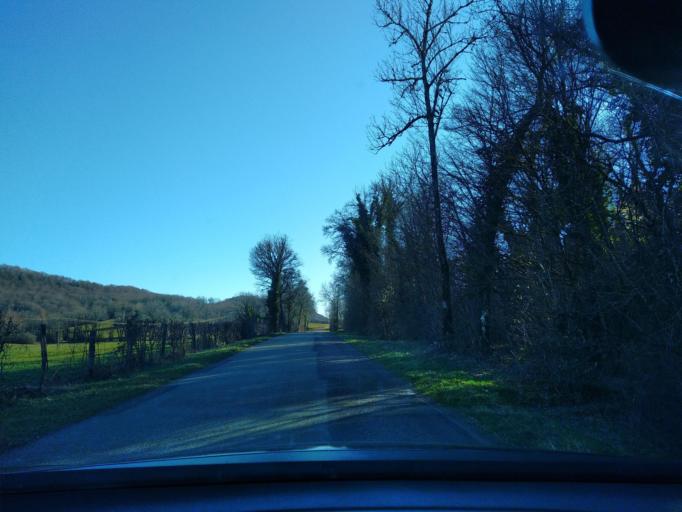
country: FR
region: Franche-Comte
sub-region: Departement du Jura
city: Poligny
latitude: 46.7162
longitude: 5.7390
